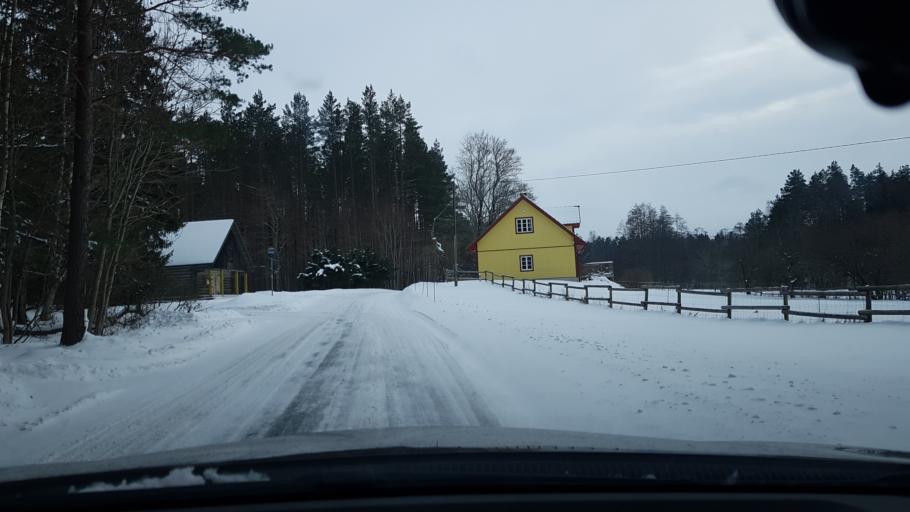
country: EE
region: Laeaene-Virumaa
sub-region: Haljala vald
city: Haljala
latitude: 59.5745
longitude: 26.1177
